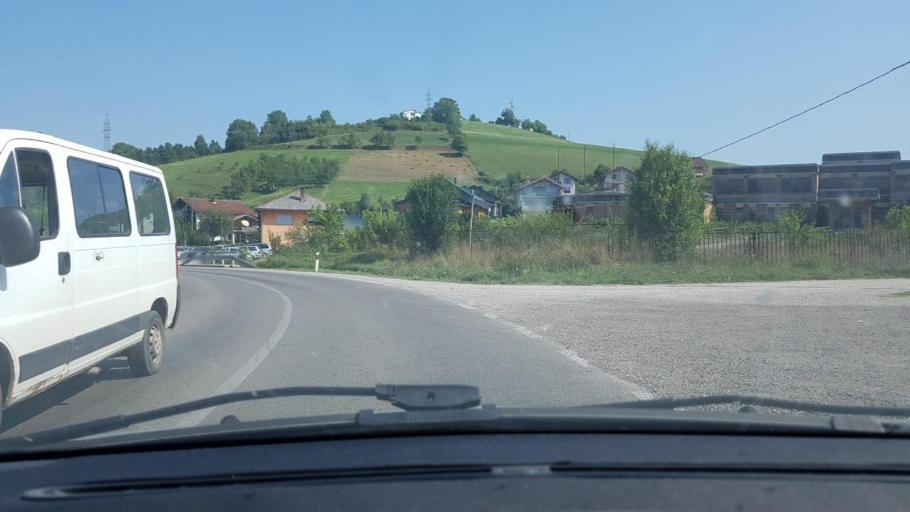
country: BA
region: Federation of Bosnia and Herzegovina
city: Mala Kladusa
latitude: 45.1540
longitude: 15.8295
